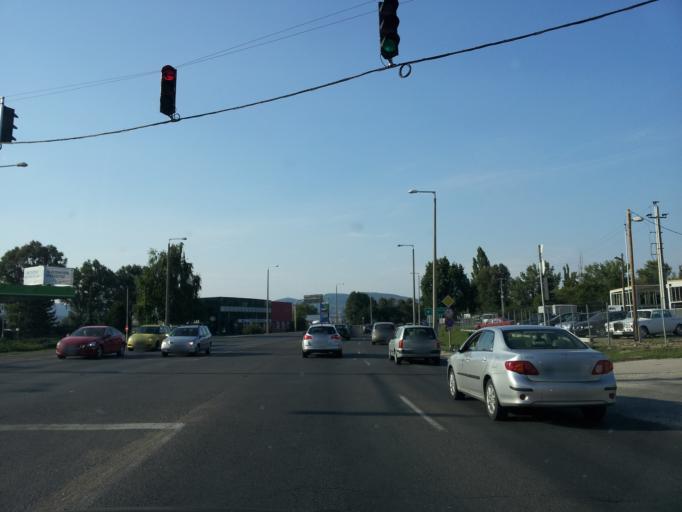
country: HU
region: Pest
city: Szentendre
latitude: 47.6414
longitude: 19.0681
